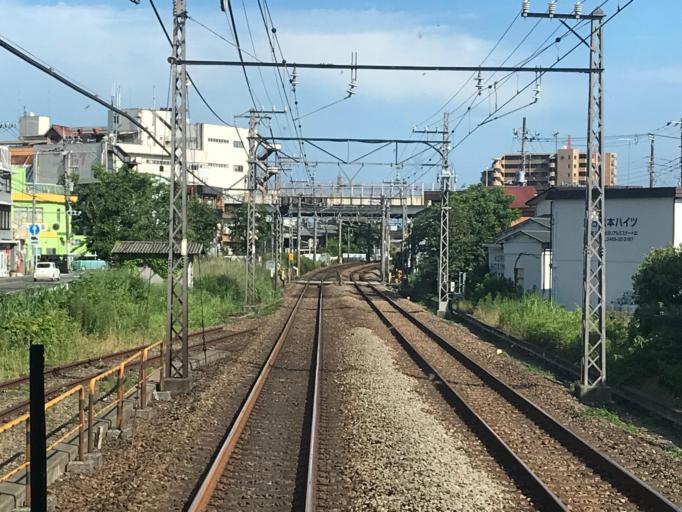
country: JP
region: Kanagawa
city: Odawara
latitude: 35.2998
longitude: 139.1444
